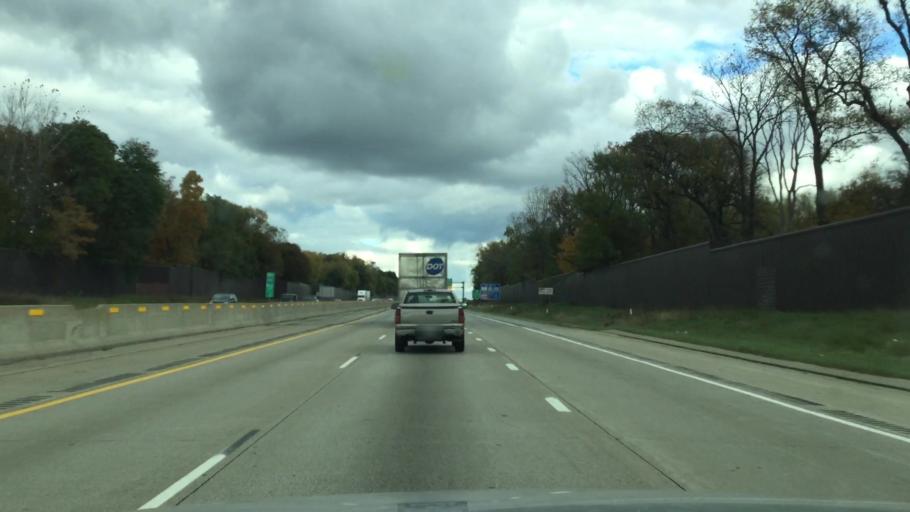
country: US
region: Michigan
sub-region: Kalamazoo County
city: Portage
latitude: 42.2408
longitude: -85.5702
